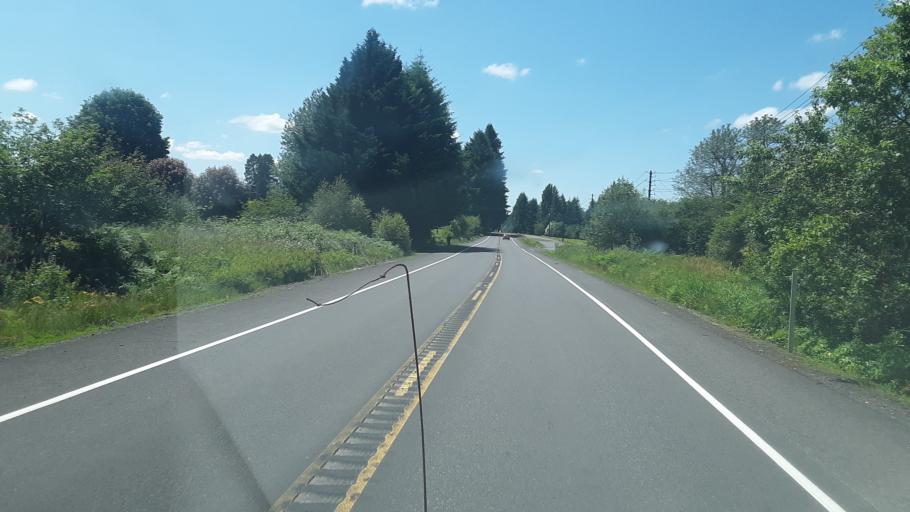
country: US
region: Washington
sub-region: Clark County
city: Amboy
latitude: 45.9243
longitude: -122.3987
